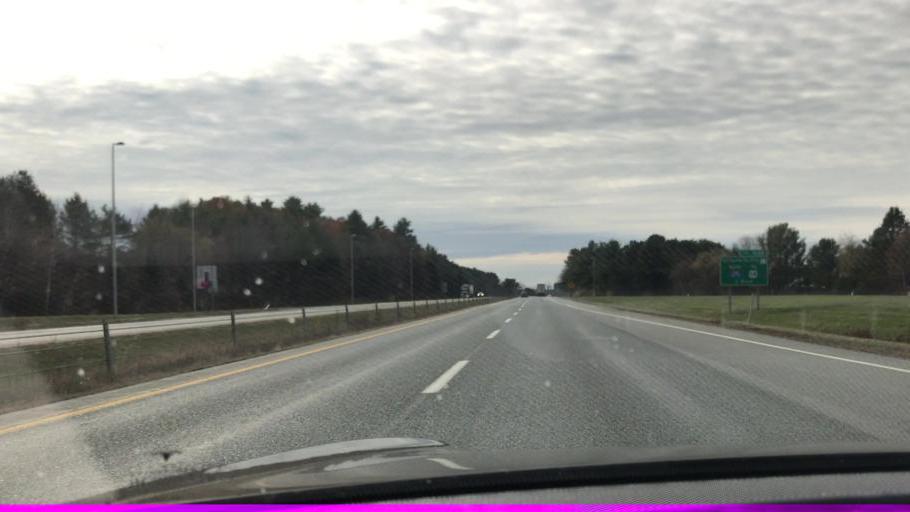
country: US
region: Maine
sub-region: Penobscot County
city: Bangor
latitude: 44.7975
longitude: -68.8024
